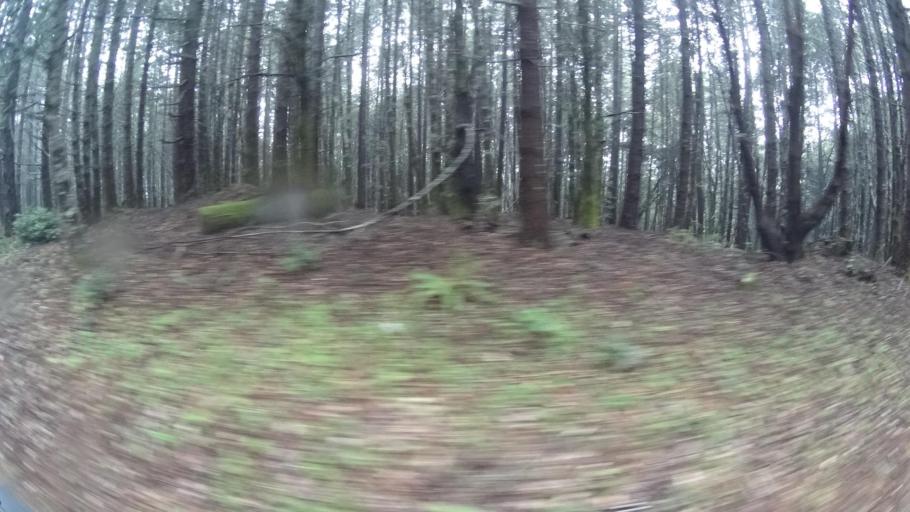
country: US
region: California
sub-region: Humboldt County
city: Westhaven-Moonstone
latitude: 41.2122
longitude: -123.9566
